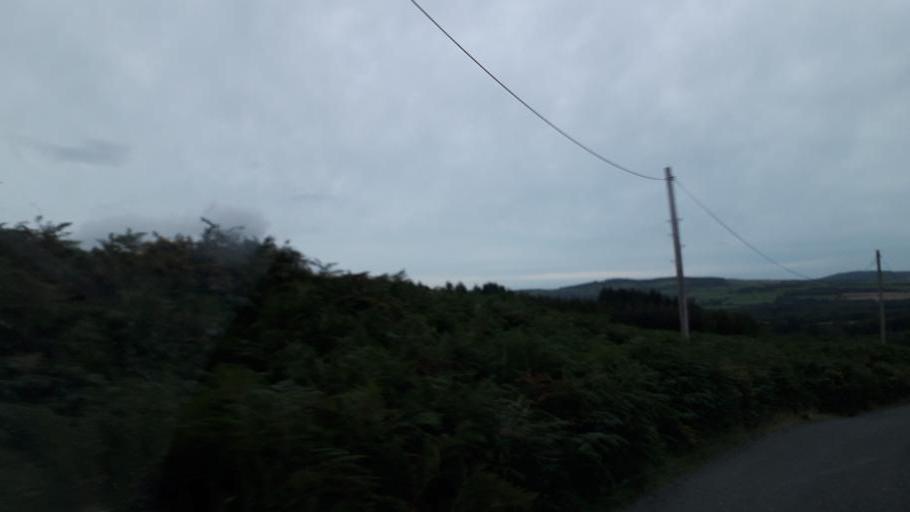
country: IE
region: Leinster
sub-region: Wicklow
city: Enniskerry
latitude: 53.0927
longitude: -6.2418
